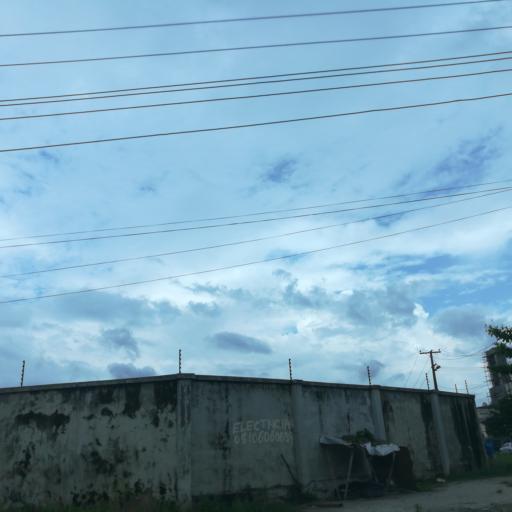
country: NG
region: Lagos
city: Ikoyi
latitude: 6.4426
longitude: 3.4688
